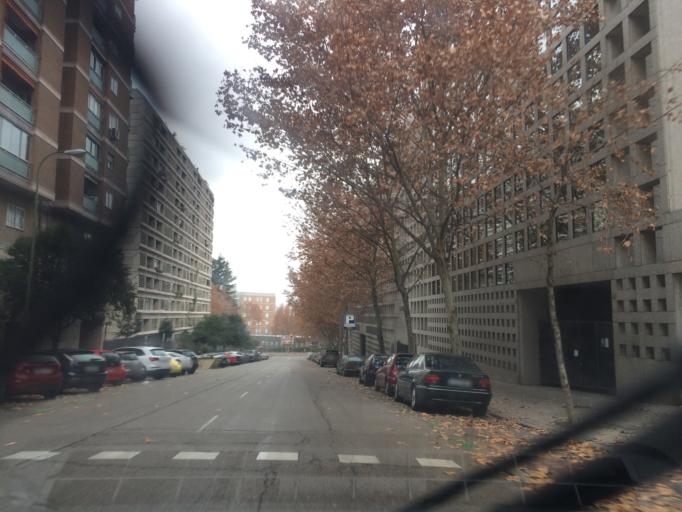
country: ES
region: Madrid
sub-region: Provincia de Madrid
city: Chamberi
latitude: 40.4480
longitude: -3.7146
